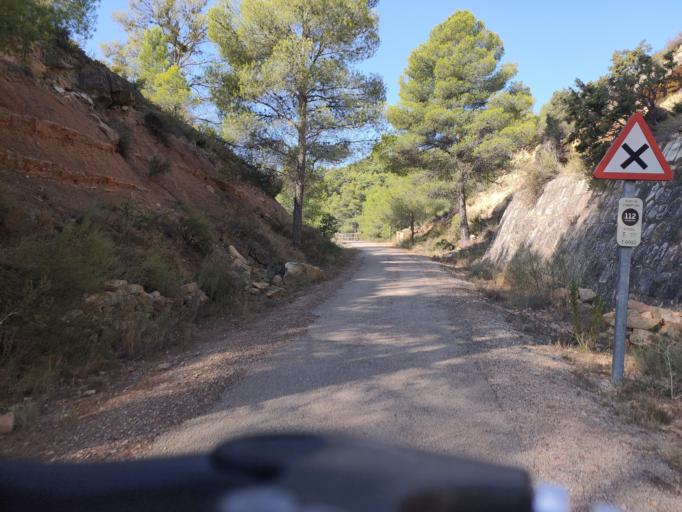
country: ES
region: Catalonia
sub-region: Provincia de Tarragona
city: Bot
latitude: 40.9985
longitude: 0.3661
